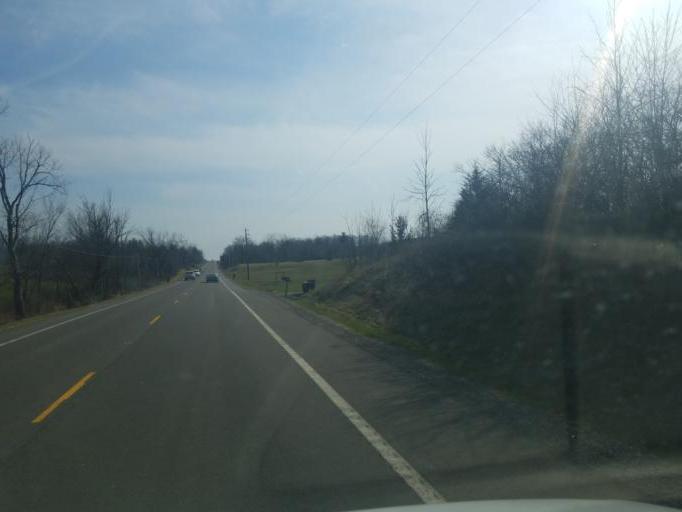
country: US
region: Ohio
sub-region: Logan County
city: Northwood
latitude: 40.4394
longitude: -83.7352
